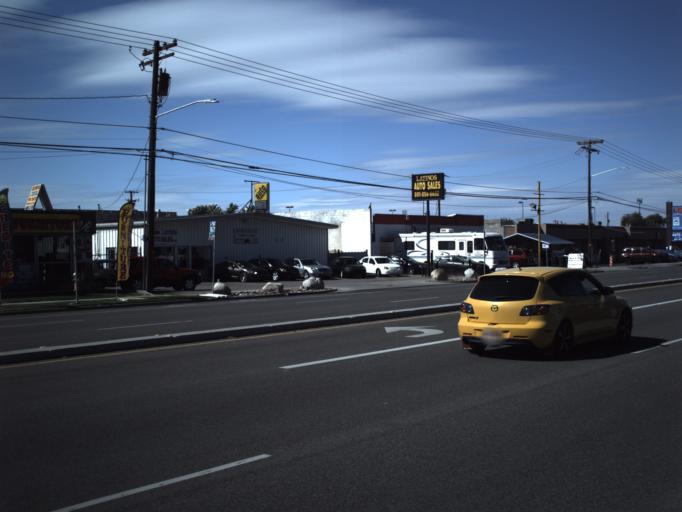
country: US
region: Utah
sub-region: Salt Lake County
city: South Salt Lake
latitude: 40.7298
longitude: -111.9389
